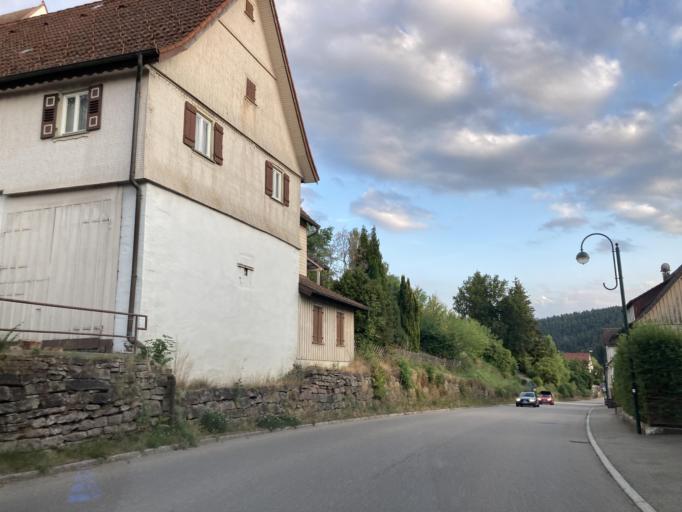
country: DE
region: Baden-Wuerttemberg
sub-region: Karlsruhe Region
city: Glatten
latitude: 48.4412
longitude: 8.5156
